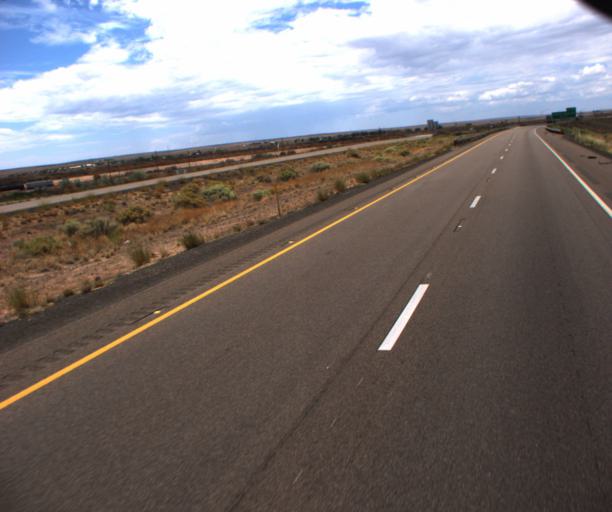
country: US
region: Arizona
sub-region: Navajo County
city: Holbrook
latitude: 34.9070
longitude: -110.1835
